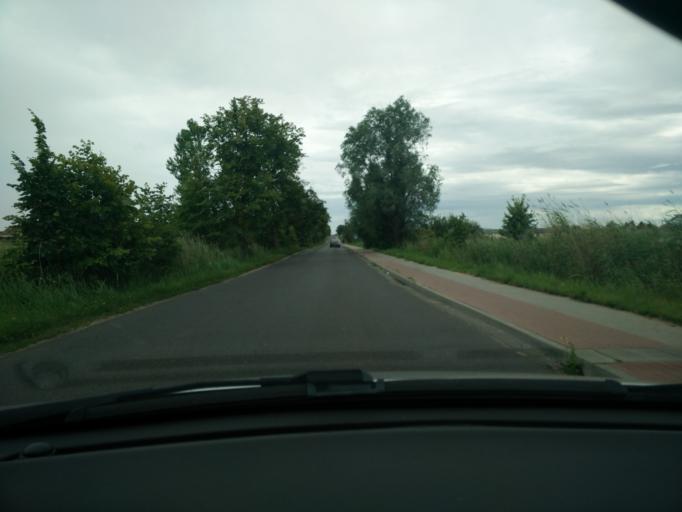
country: PL
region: Pomeranian Voivodeship
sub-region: Powiat pucki
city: Mosty
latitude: 54.6254
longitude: 18.4966
